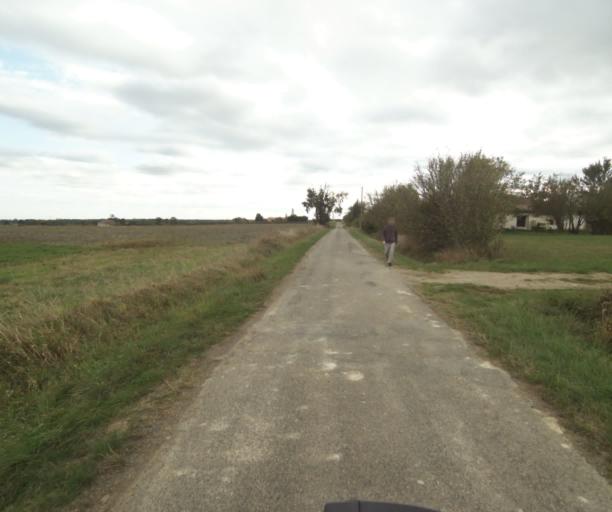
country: FR
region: Midi-Pyrenees
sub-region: Departement du Tarn-et-Garonne
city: Verdun-sur-Garonne
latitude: 43.8647
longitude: 1.1625
